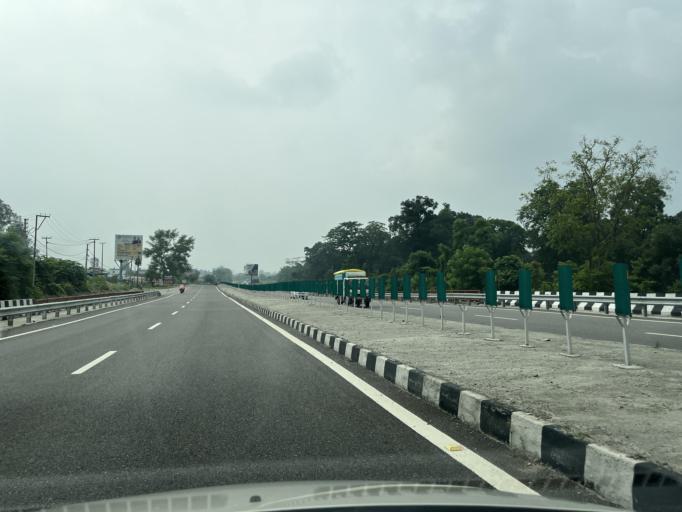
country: IN
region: Uttarakhand
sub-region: Dehradun
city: Raiwala
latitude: 30.0637
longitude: 78.2104
